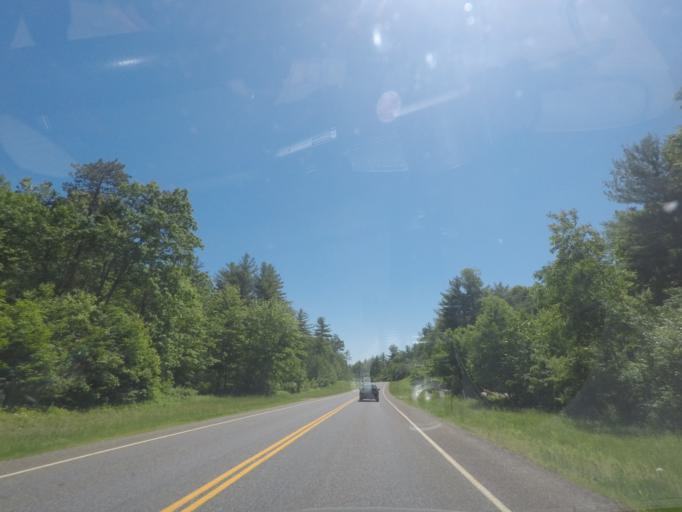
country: US
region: New York
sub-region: Saratoga County
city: Mechanicville
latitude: 42.9472
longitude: -73.7401
